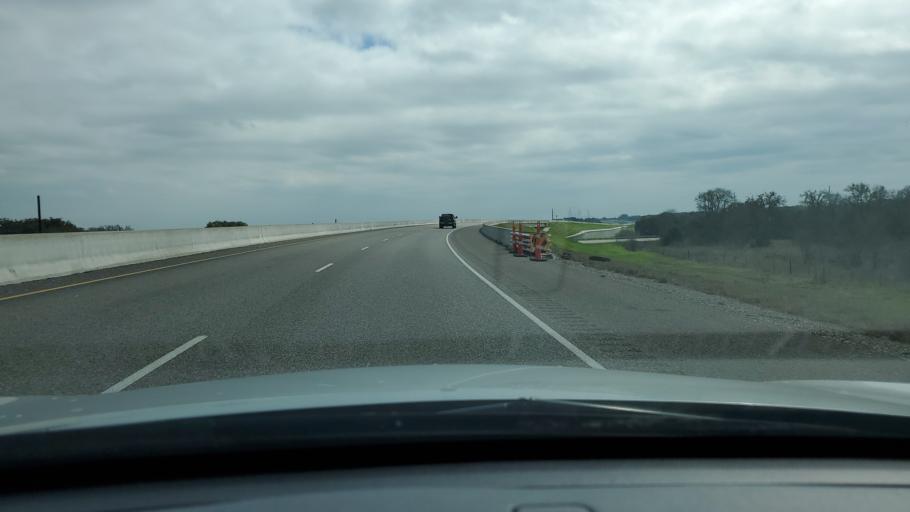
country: US
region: Texas
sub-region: Williamson County
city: Serenada
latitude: 30.7579
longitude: -97.7222
